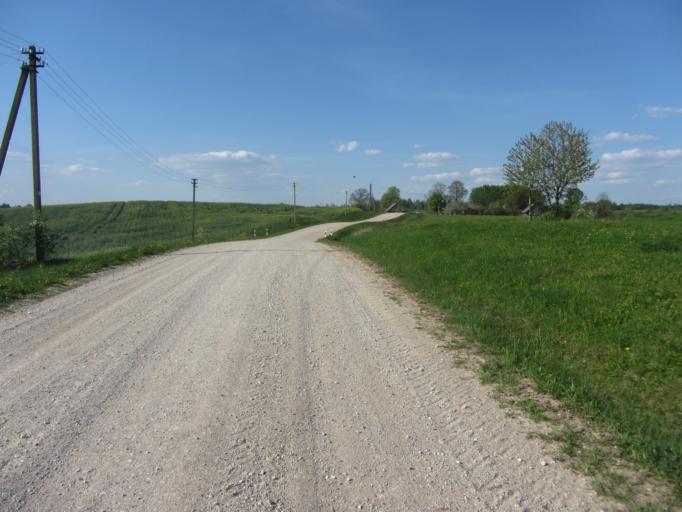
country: LT
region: Utenos apskritis
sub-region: Anyksciai
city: Anyksciai
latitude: 55.3282
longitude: 25.0717
